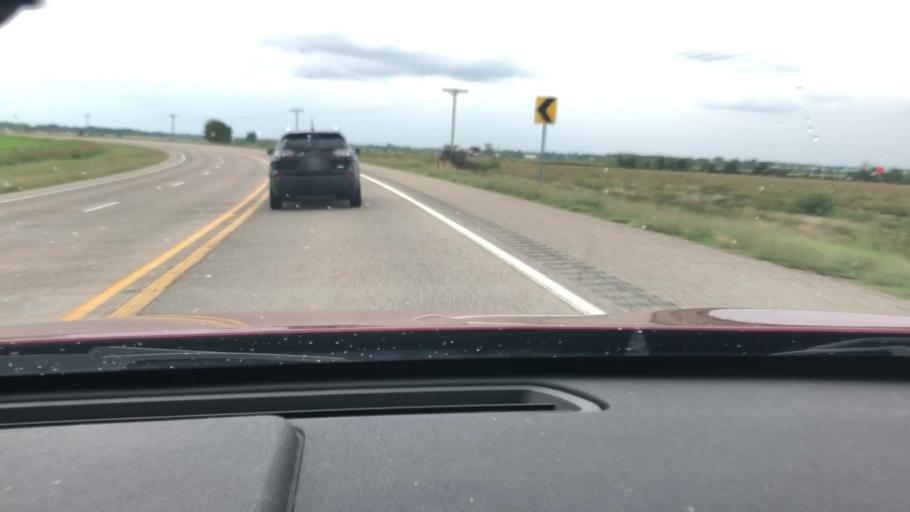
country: US
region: Arkansas
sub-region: Lafayette County
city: Lewisville
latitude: 33.3962
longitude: -93.7446
